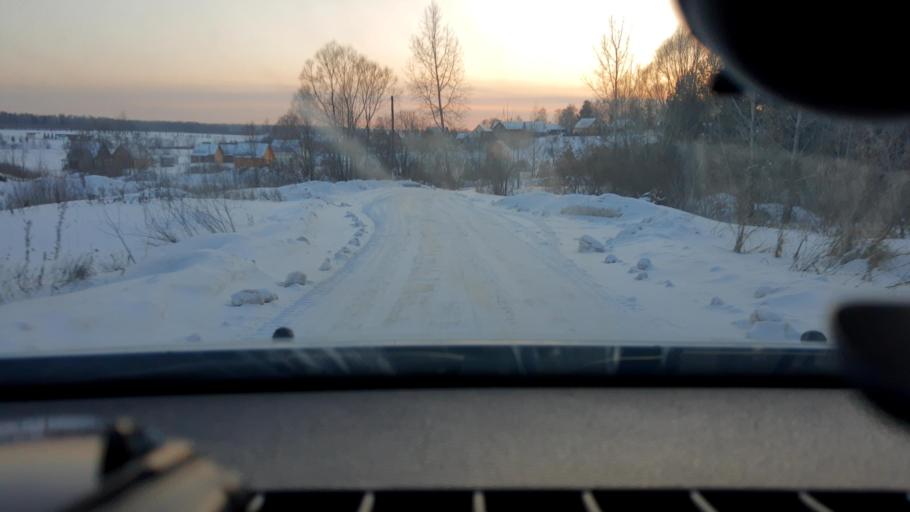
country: RU
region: Bashkortostan
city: Iglino
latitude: 54.8571
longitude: 56.4638
